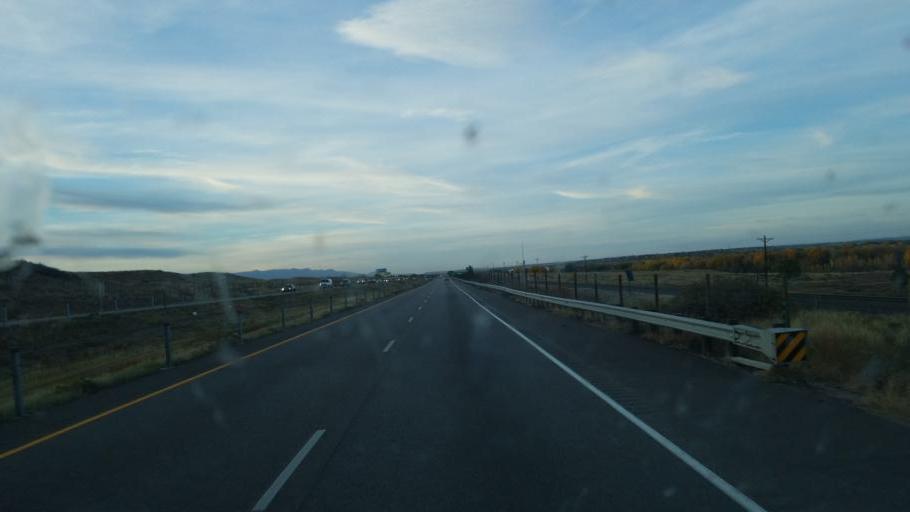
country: US
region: Colorado
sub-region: El Paso County
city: Fountain
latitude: 38.6504
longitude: -104.6963
